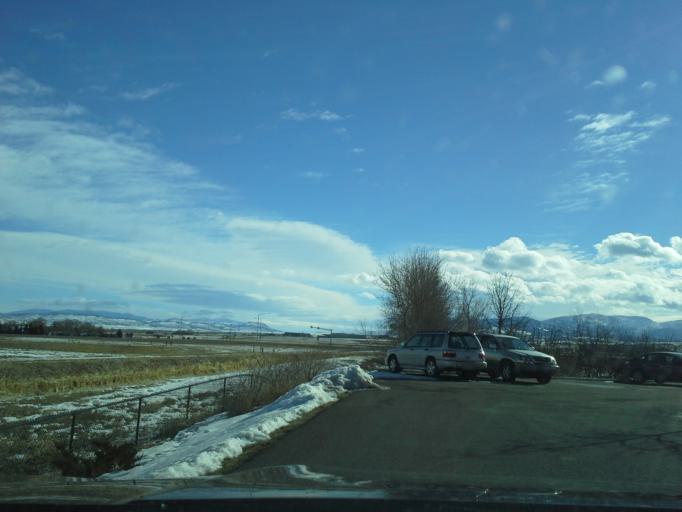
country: US
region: Montana
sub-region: Lewis and Clark County
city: Helena
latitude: 46.6177
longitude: -111.9953
